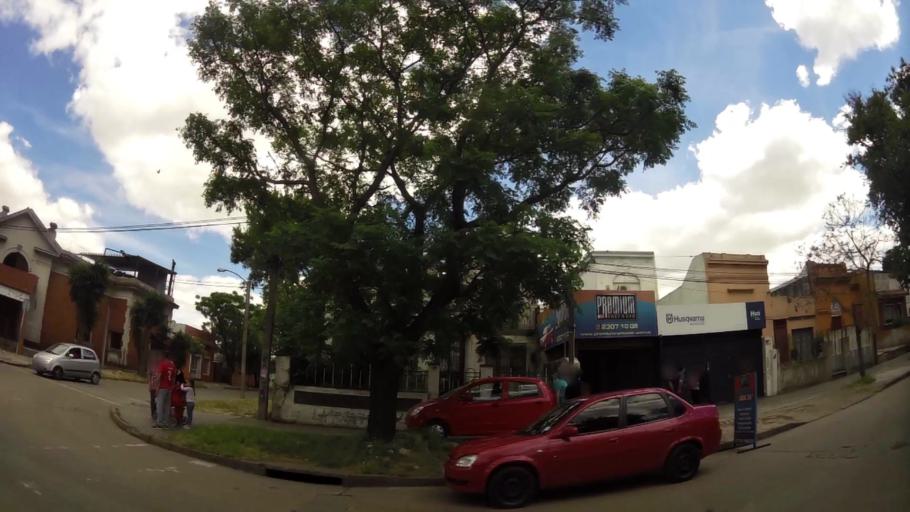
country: UY
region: Montevideo
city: Montevideo
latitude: -34.8603
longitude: -56.2290
